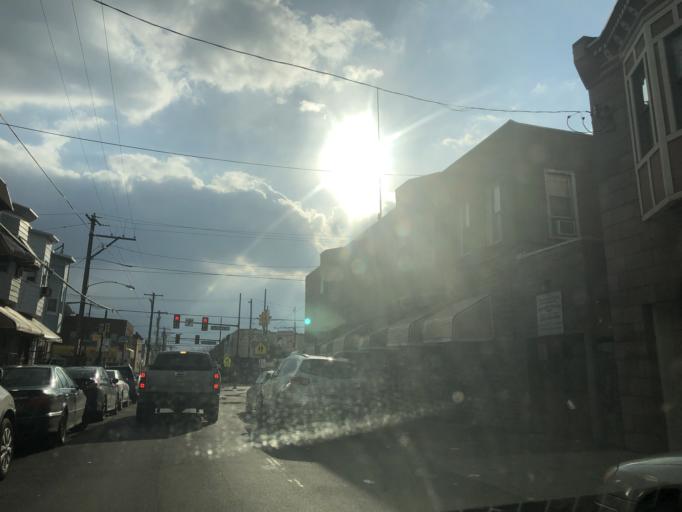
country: US
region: Pennsylvania
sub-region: Philadelphia County
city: Philadelphia
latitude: 39.9246
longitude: -75.1779
